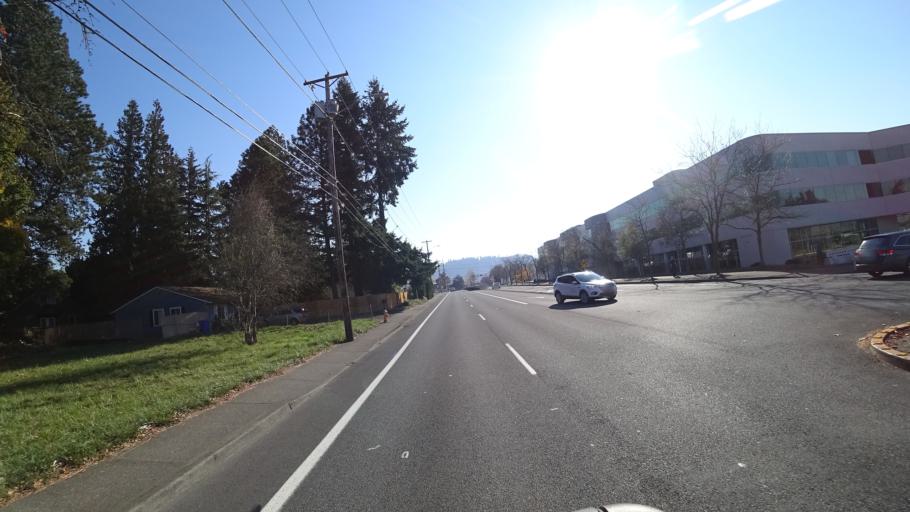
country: US
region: Oregon
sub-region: Multnomah County
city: Gresham
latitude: 45.5072
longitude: -122.4353
